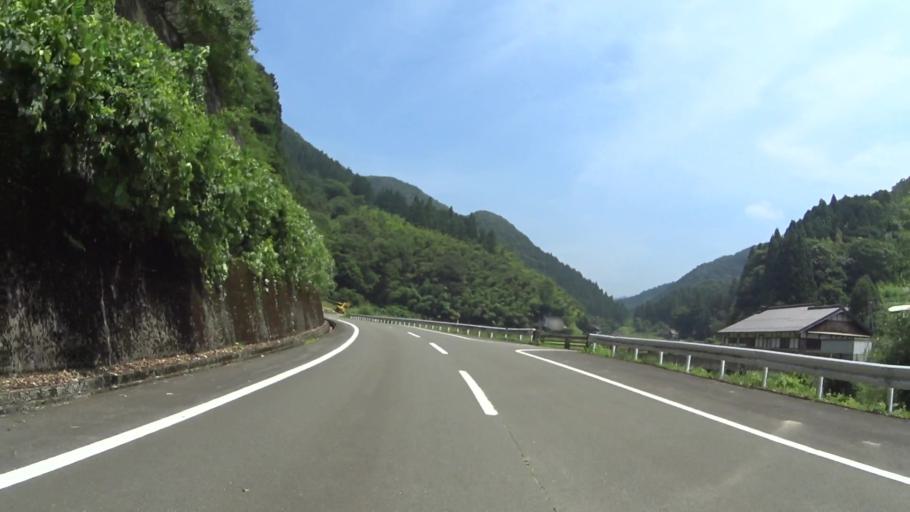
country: JP
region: Kyoto
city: Maizuru
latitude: 35.3049
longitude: 135.4278
